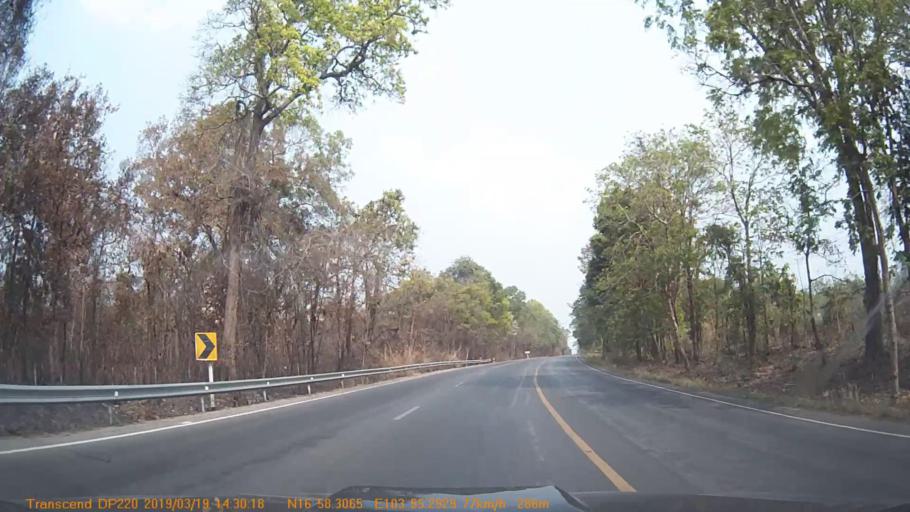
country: TH
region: Sakon Nakhon
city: Phu Phan
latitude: 16.9718
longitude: 103.9220
